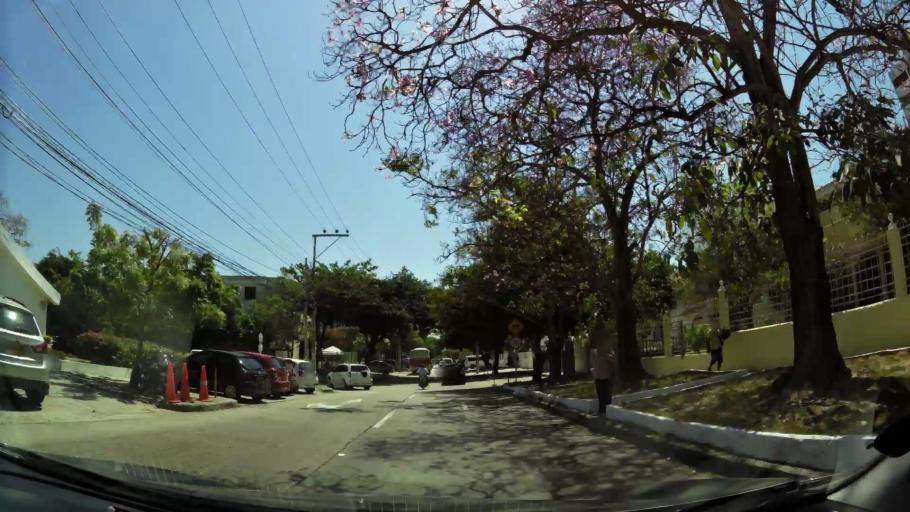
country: CO
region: Atlantico
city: Barranquilla
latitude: 11.0032
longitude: -74.7986
